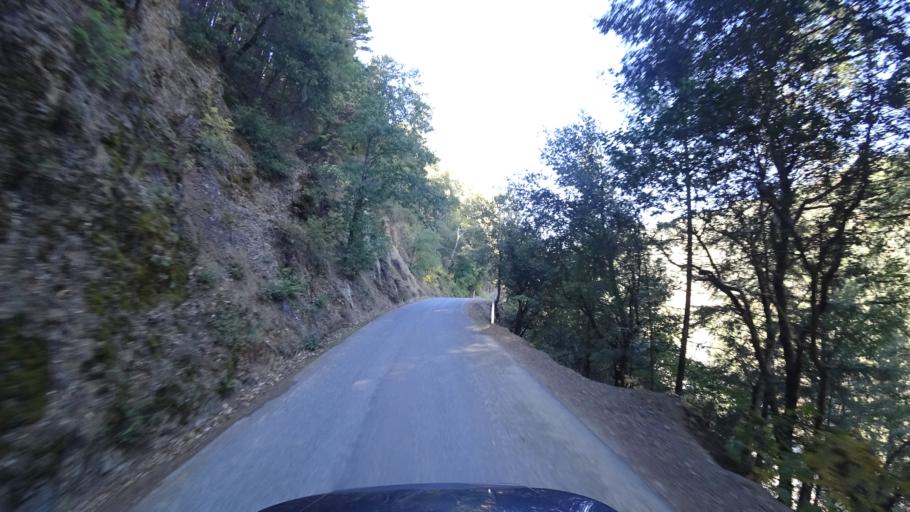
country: US
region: California
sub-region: Humboldt County
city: Willow Creek
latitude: 41.2435
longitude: -123.2969
